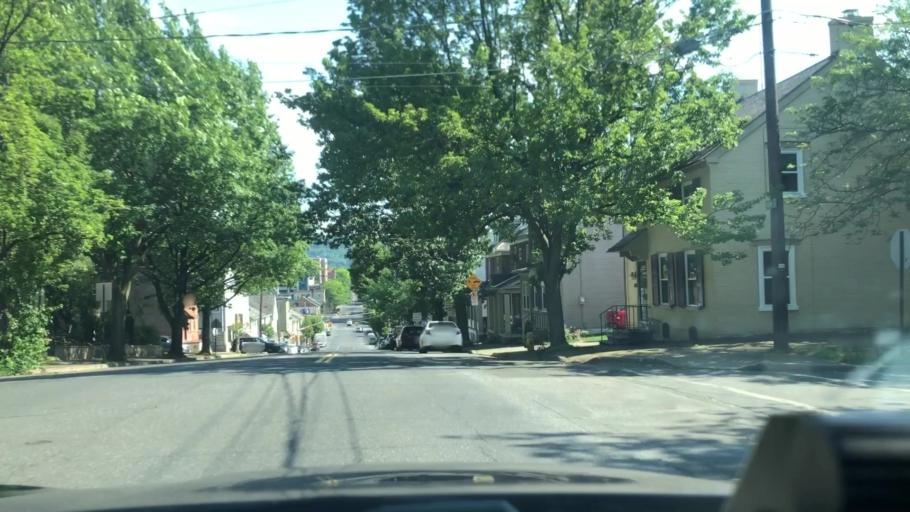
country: US
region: Pennsylvania
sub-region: Northampton County
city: Bethlehem
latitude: 40.6279
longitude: -75.3818
